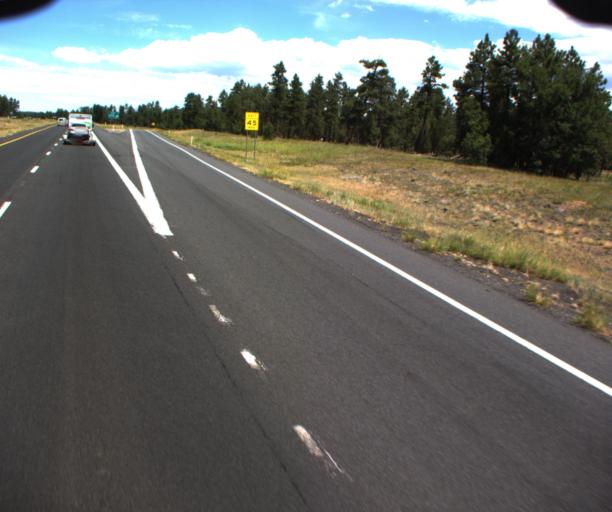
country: US
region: Arizona
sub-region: Coconino County
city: Sedona
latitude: 34.8493
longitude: -111.6050
